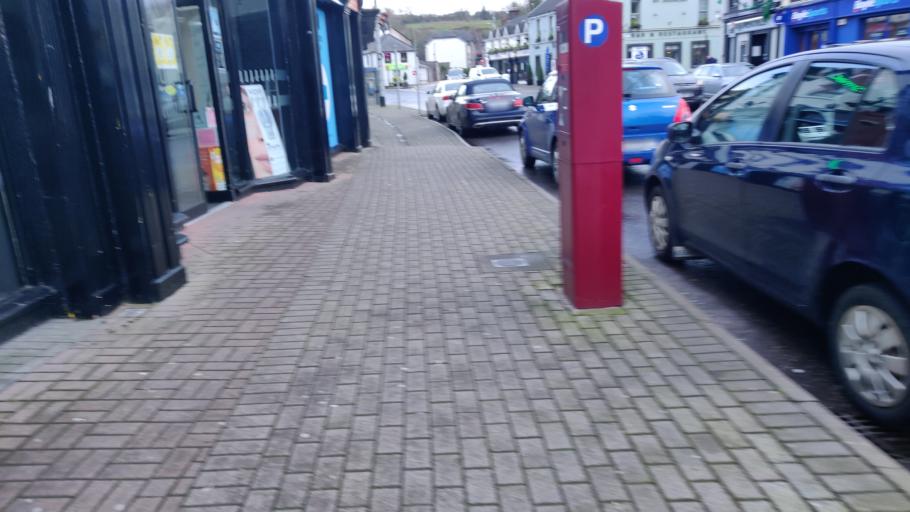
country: IE
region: Munster
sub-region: County Cork
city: Cork
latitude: 51.8777
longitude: -8.4364
